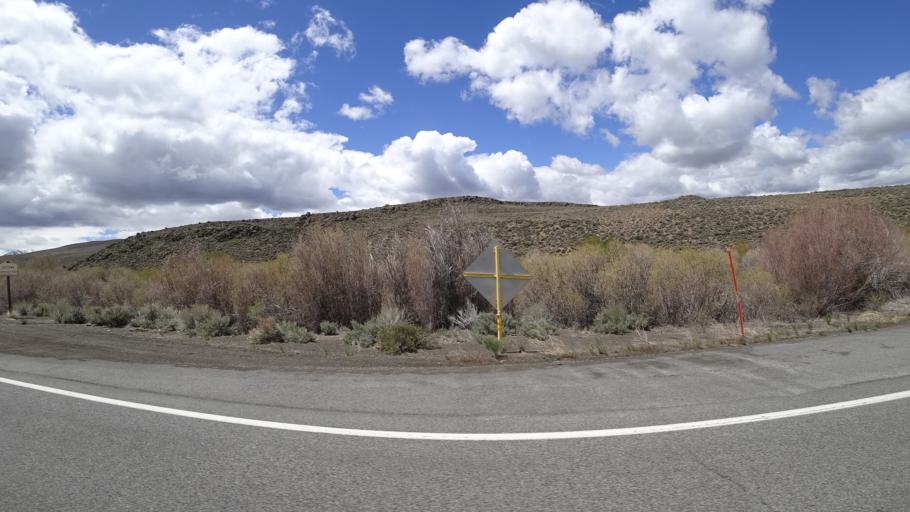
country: US
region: California
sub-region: Mono County
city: Bridgeport
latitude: 38.1736
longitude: -119.1945
